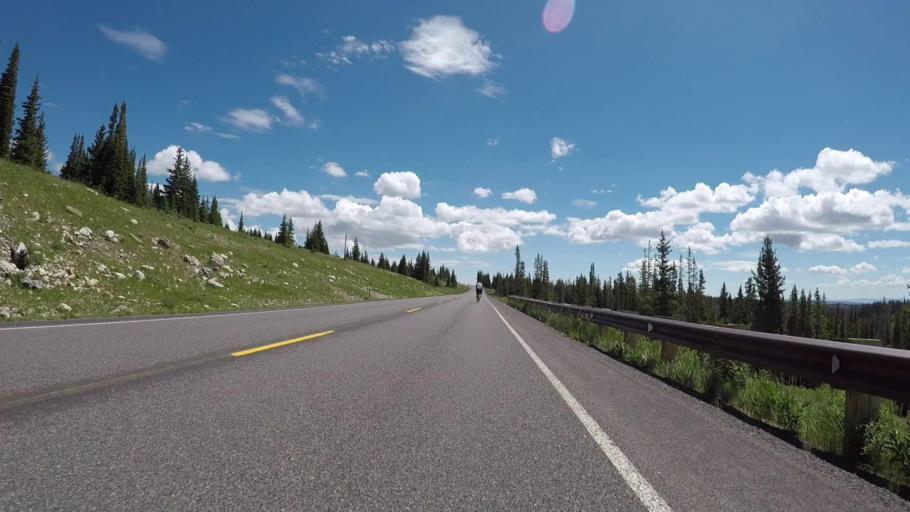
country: US
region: Wyoming
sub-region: Carbon County
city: Saratoga
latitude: 41.3511
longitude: -106.2793
